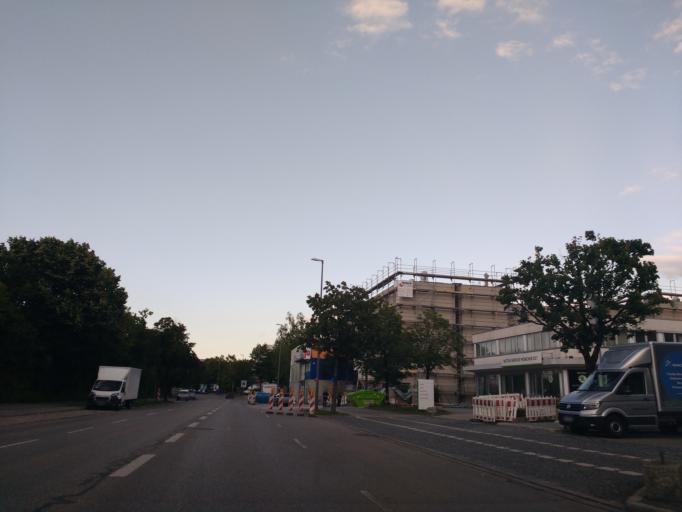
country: DE
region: Bavaria
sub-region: Upper Bavaria
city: Bogenhausen
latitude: 48.1346
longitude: 11.6644
